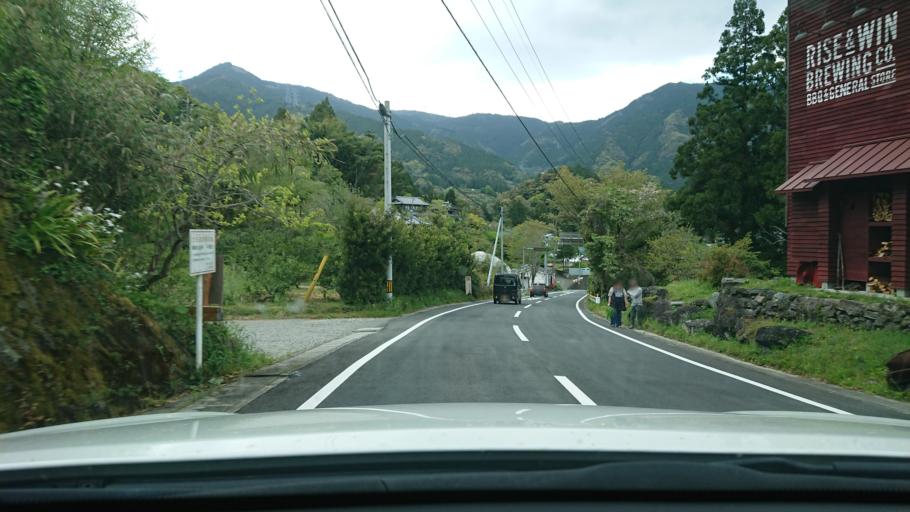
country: JP
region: Tokushima
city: Ishii
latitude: 33.9191
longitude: 134.4264
